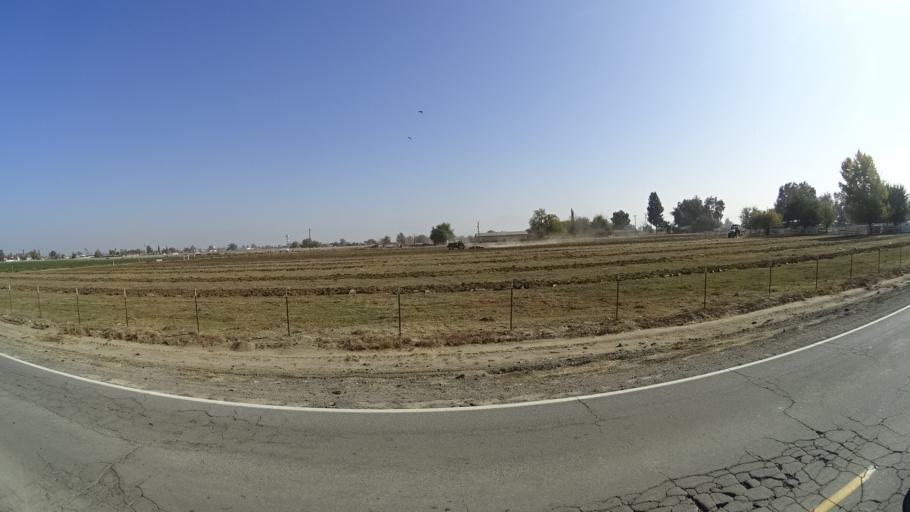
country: US
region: California
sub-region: Kern County
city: Greenfield
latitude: 35.2608
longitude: -119.0393
